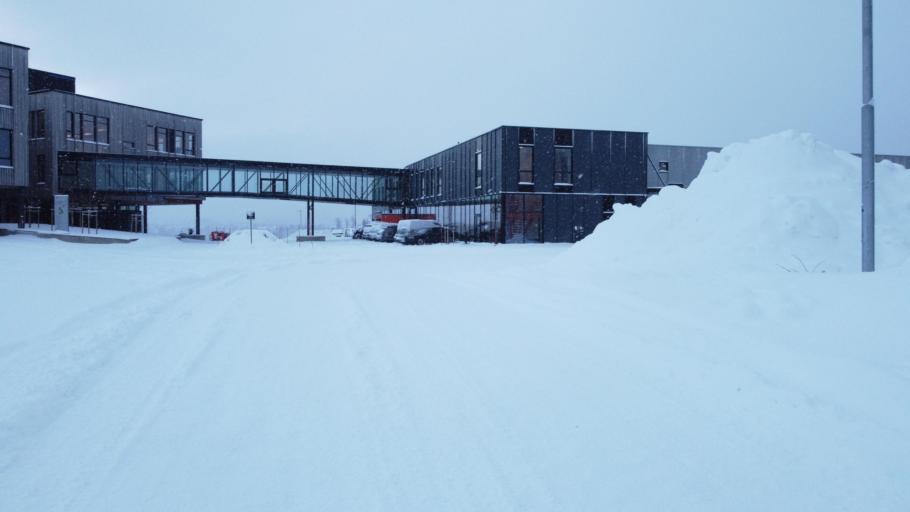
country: NO
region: Nordland
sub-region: Rana
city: Mo i Rana
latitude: 66.3306
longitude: 14.1562
